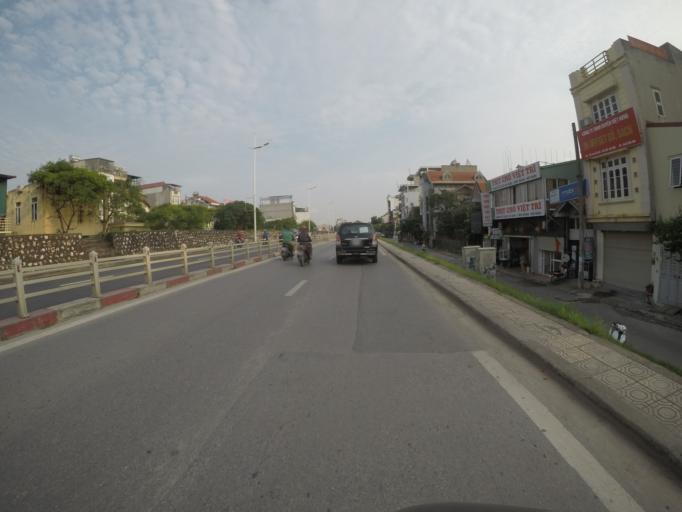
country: VN
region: Ha Noi
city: Tay Ho
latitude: 21.0783
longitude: 105.8200
